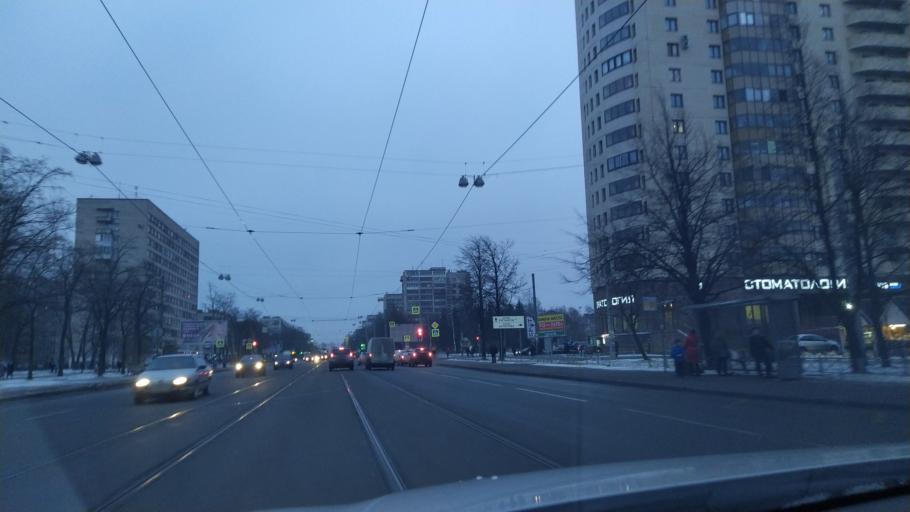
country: RU
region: Leningrad
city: Akademicheskoe
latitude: 60.0114
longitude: 30.4042
